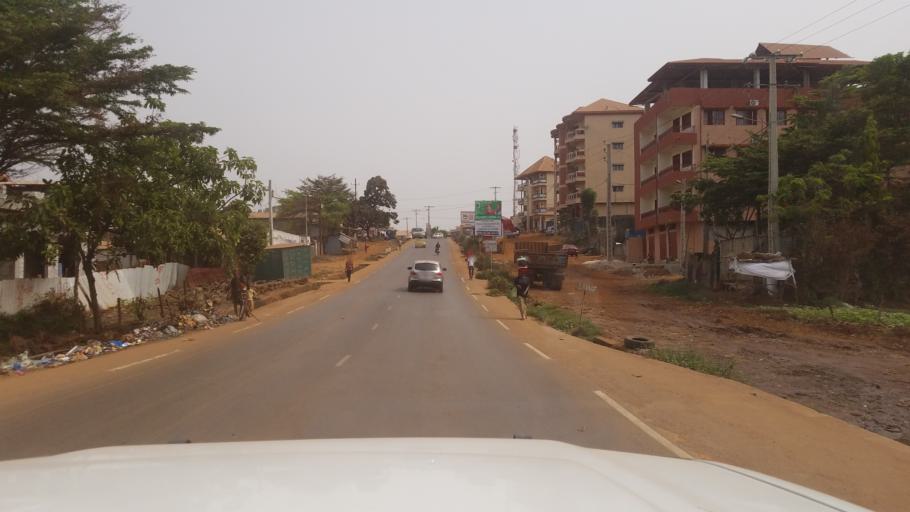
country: GN
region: Kindia
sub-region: Prefecture de Dubreka
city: Dubreka
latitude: 9.6628
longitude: -13.5943
